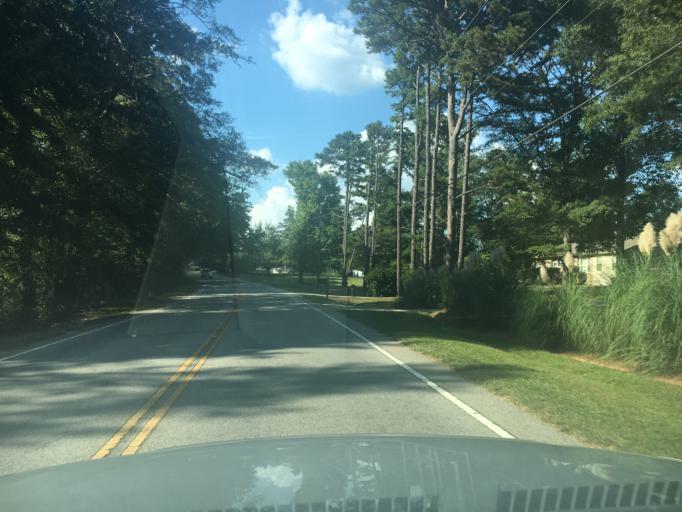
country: US
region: South Carolina
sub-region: Greenville County
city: Fountain Inn
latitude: 34.6565
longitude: -82.2579
